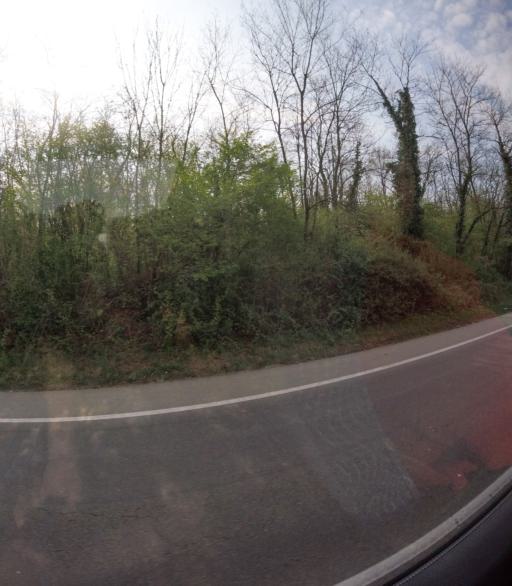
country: IT
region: Piedmont
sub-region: Provincia di Novara
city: Paruzzaro
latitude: 45.7320
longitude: 8.5008
